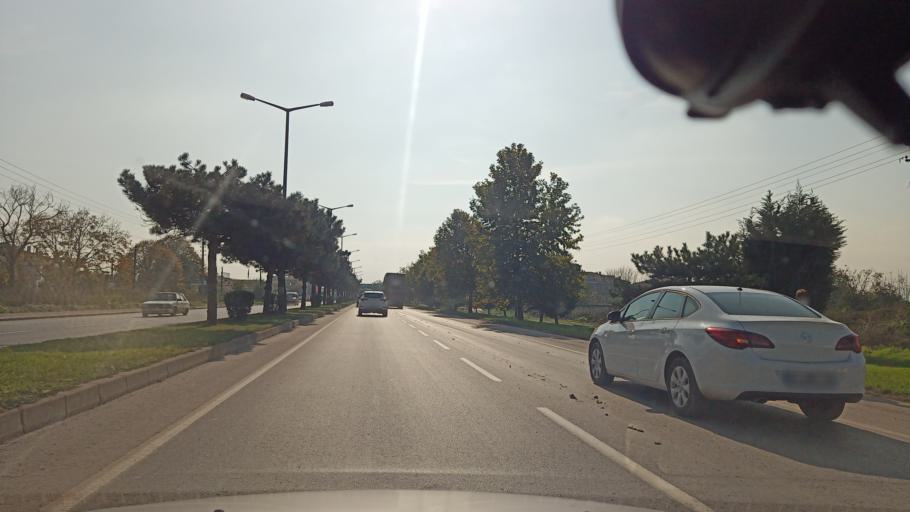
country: TR
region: Sakarya
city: Adapazari
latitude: 40.8062
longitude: 30.4057
